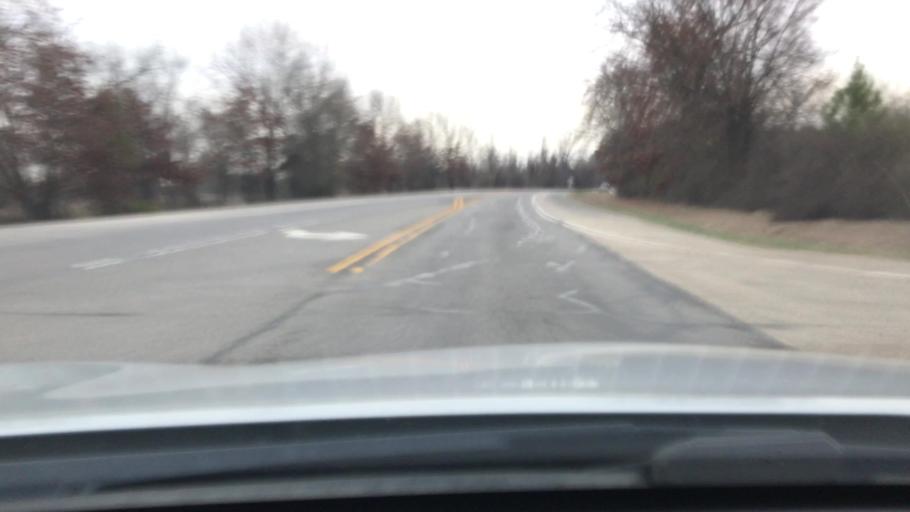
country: US
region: Arkansas
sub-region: Hempstead County
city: Hope
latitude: 33.6866
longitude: -93.5787
